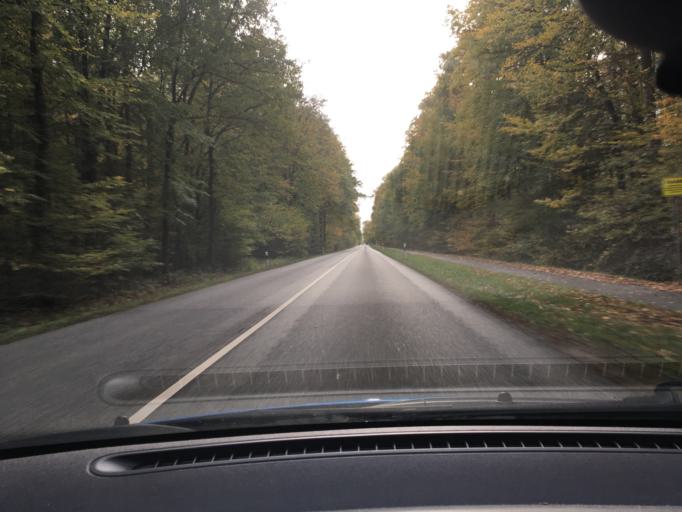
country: DE
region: Schleswig-Holstein
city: Sahms
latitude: 53.5392
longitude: 10.5308
